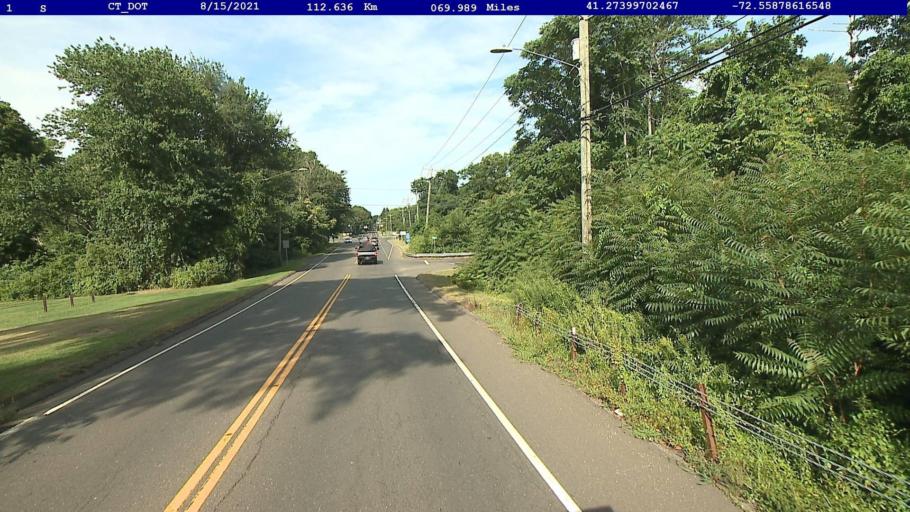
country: US
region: Connecticut
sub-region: Middlesex County
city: Clinton
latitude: 41.2740
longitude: -72.5588
